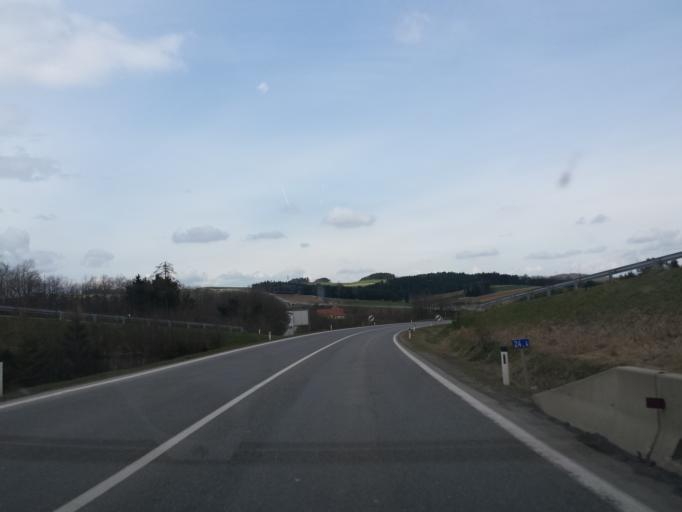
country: AT
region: Lower Austria
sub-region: Politischer Bezirk Krems
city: Jaidhof
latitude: 48.5266
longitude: 15.4367
